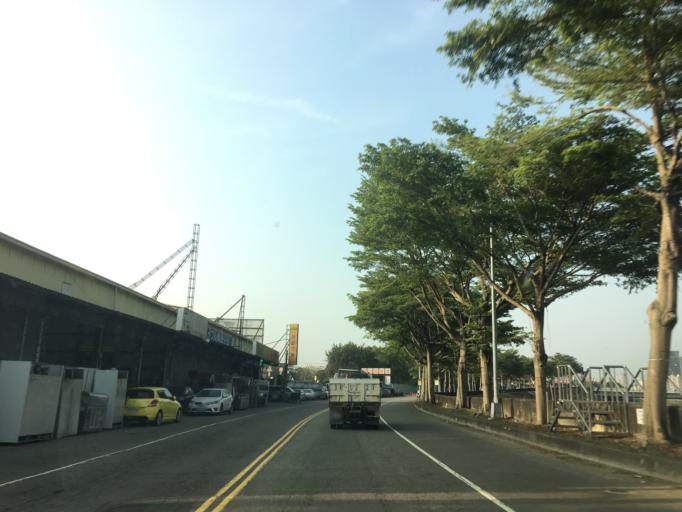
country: TW
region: Taiwan
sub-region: Taichung City
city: Taichung
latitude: 24.1623
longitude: 120.7035
